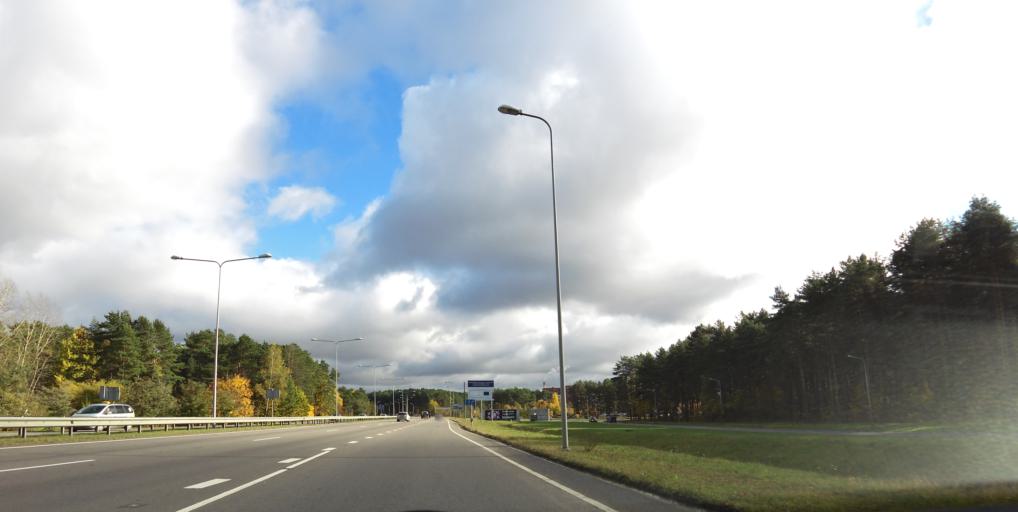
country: LT
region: Vilnius County
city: Lazdynai
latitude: 54.6705
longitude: 25.2033
